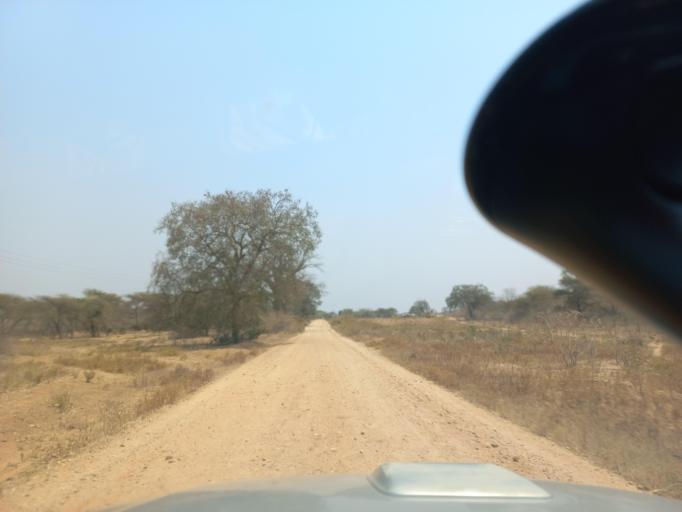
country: ZW
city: Chirundu
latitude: -15.9340
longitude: 28.8632
